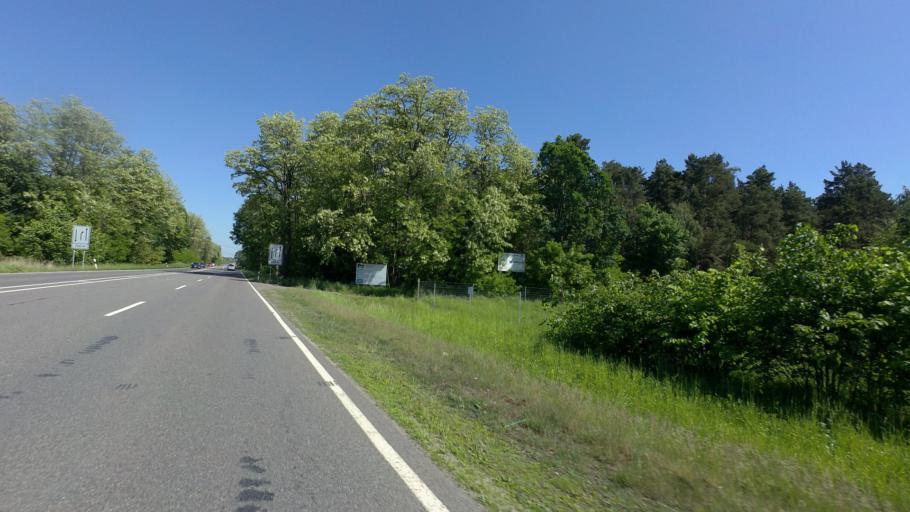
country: DE
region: Brandenburg
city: Spremberg
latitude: 51.6192
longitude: 14.3629
